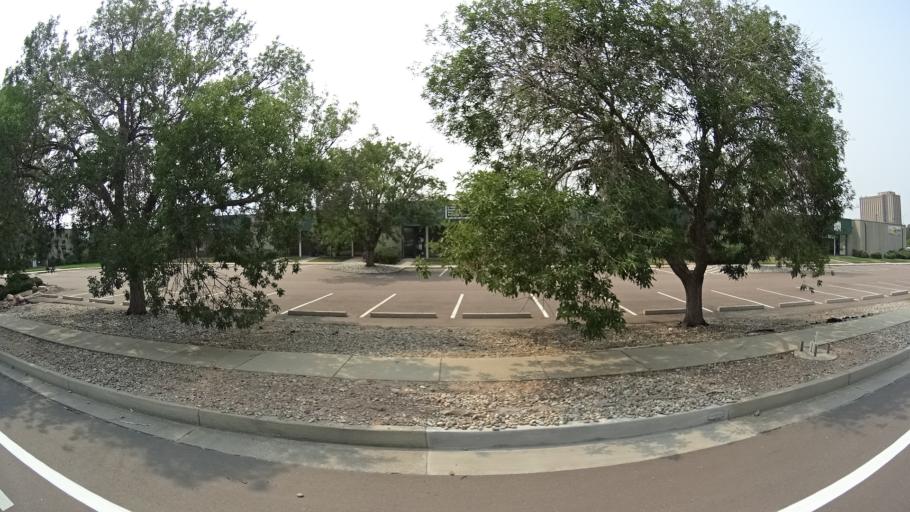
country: US
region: Colorado
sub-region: El Paso County
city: Stratmoor
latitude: 38.7945
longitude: -104.7899
